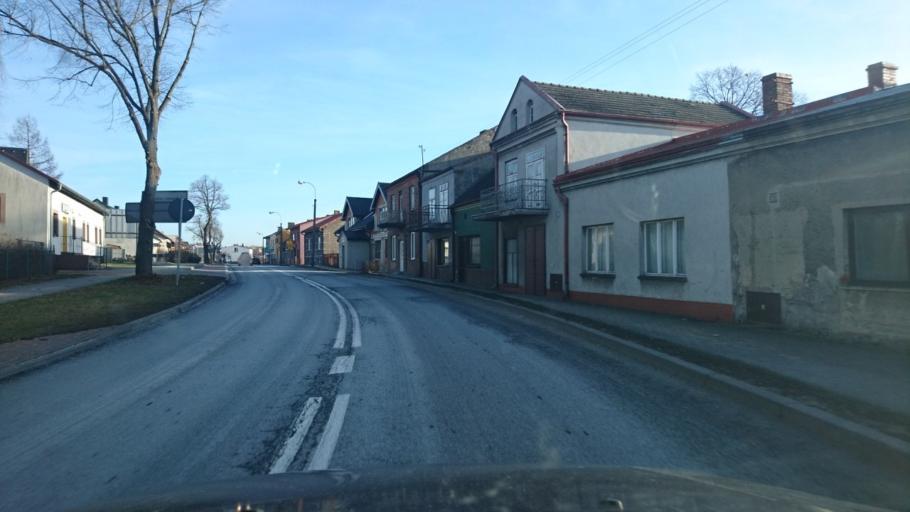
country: PL
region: Opole Voivodeship
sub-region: Powiat oleski
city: Dalachow
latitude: 51.0381
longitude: 18.5989
